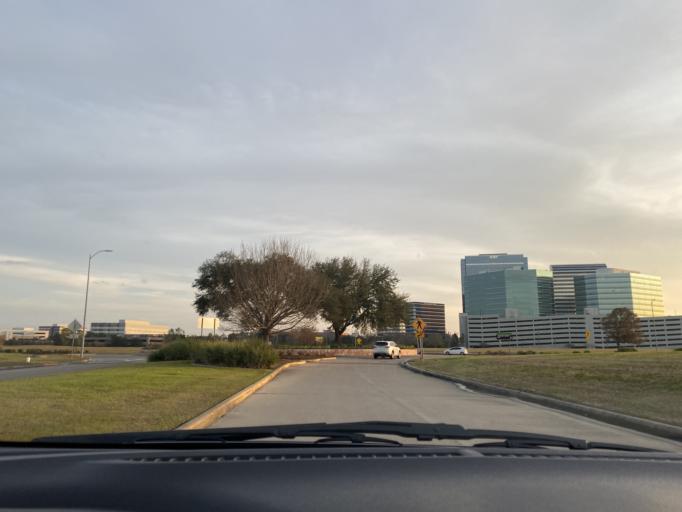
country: US
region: Texas
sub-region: Harris County
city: Bunker Hill Village
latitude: 29.7323
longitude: -95.5552
